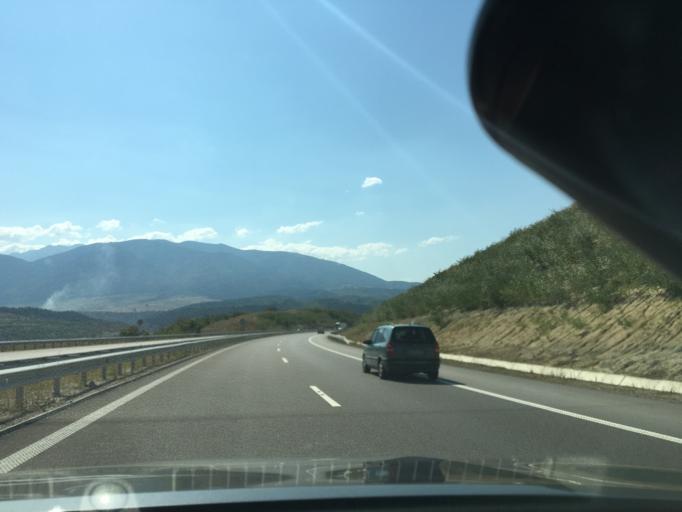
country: BG
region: Kyustendil
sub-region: Obshtina Dupnitsa
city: Dupnitsa
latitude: 42.2542
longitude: 23.0816
